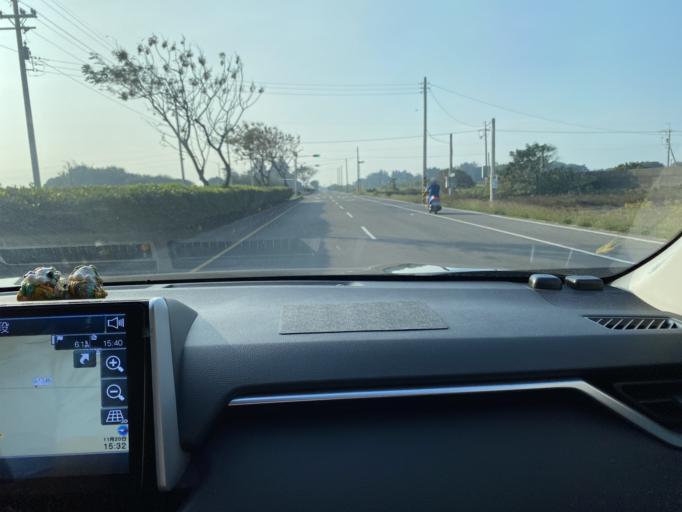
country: TW
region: Taiwan
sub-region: Changhua
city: Chang-hua
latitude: 23.9595
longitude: 120.3979
